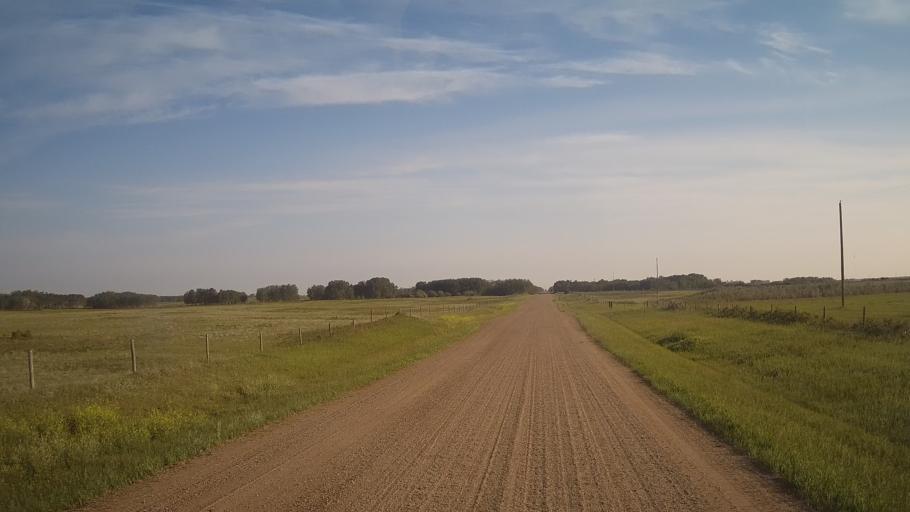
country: CA
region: Saskatchewan
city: Saskatoon
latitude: 51.8245
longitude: -106.5239
